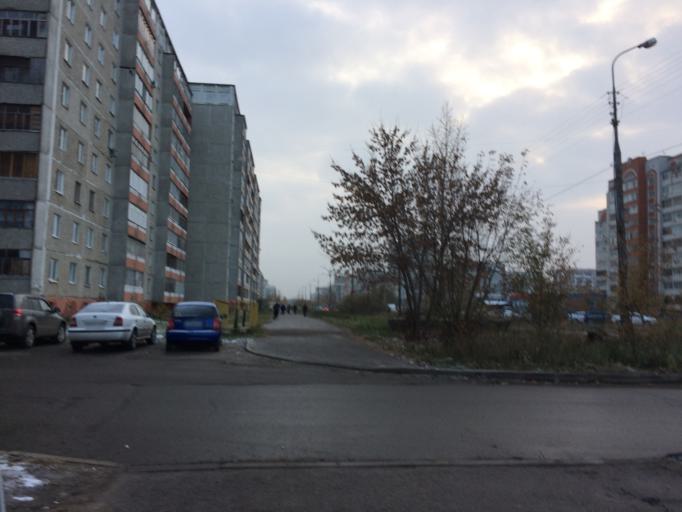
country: RU
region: Mariy-El
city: Yoshkar-Ola
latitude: 56.6382
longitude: 47.9235
